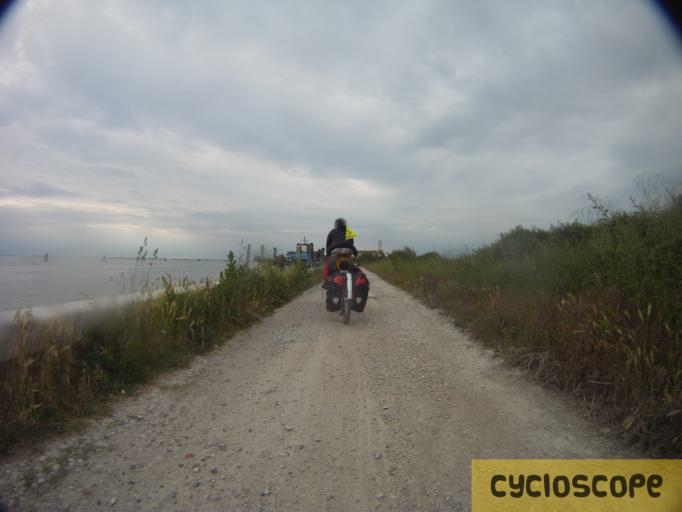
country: IT
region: Veneto
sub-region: Provincia di Venezia
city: San Pietro in Volta
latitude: 45.3066
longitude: 12.3102
